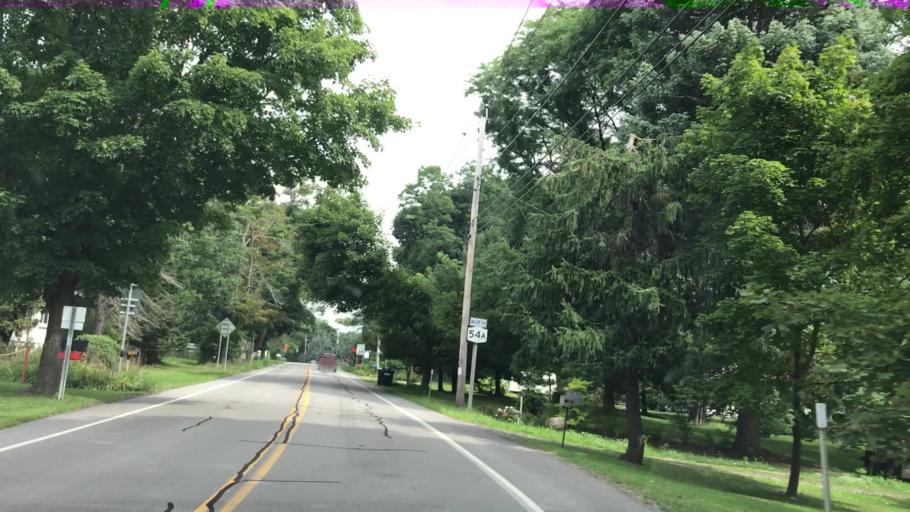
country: US
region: New York
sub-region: Steuben County
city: Sylvan Beach
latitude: 42.5290
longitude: -77.1526
